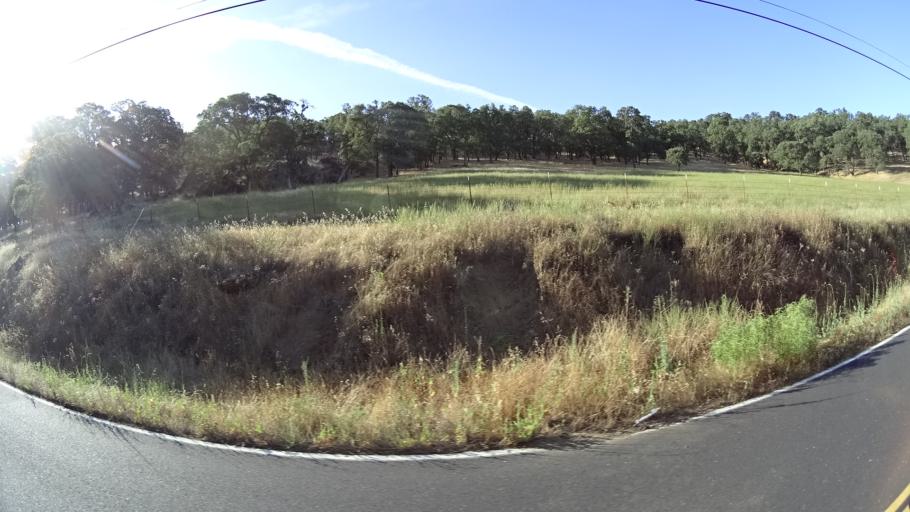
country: US
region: California
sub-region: Calaveras County
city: Valley Springs
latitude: 38.2120
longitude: -120.7766
